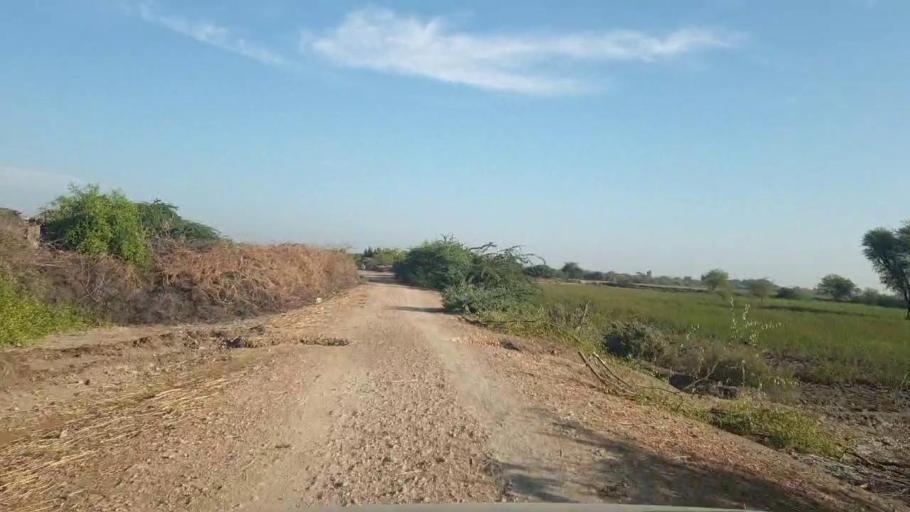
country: PK
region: Sindh
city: Talhar
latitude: 24.8290
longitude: 68.8402
